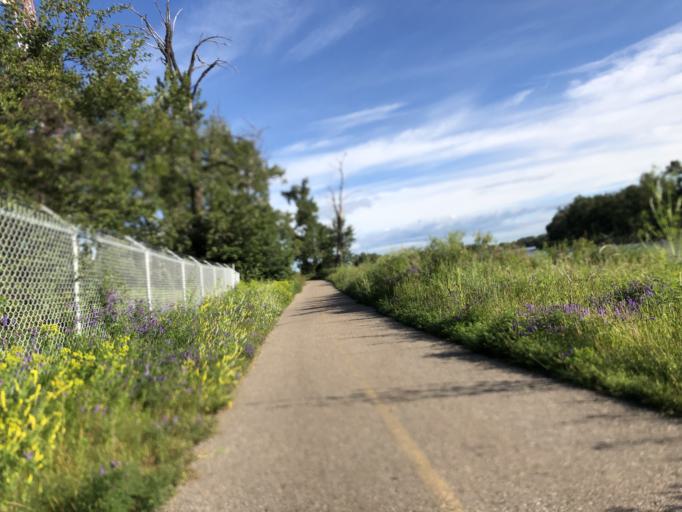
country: CA
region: Alberta
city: Calgary
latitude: 50.9553
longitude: -114.0230
